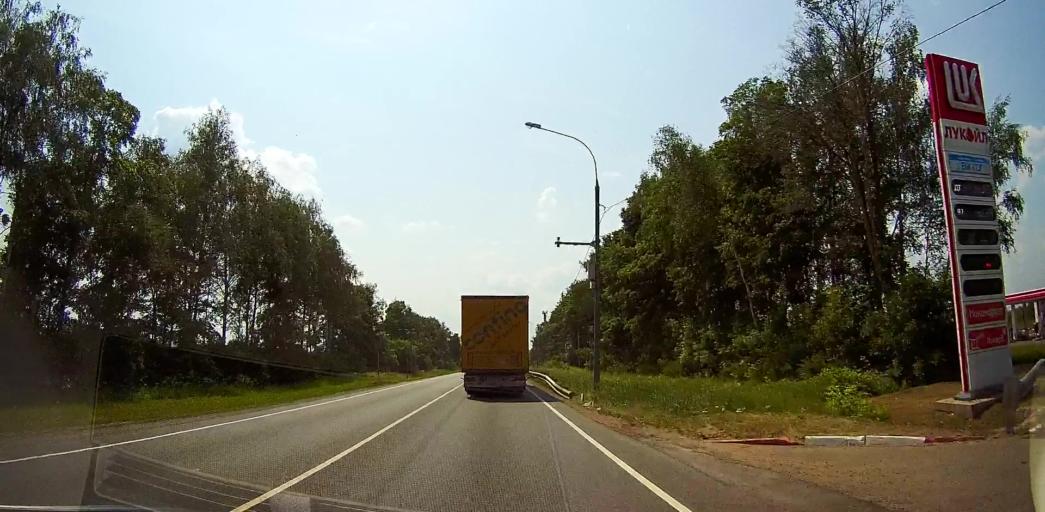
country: RU
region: Moskovskaya
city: Meshcherino
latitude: 55.1999
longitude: 38.3726
